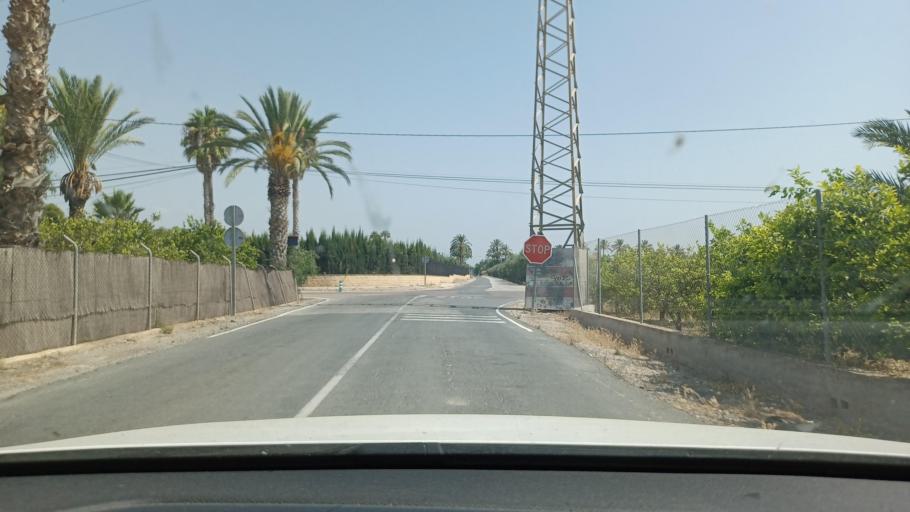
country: ES
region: Valencia
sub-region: Provincia de Alicante
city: Elche
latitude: 38.2293
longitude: -0.6941
